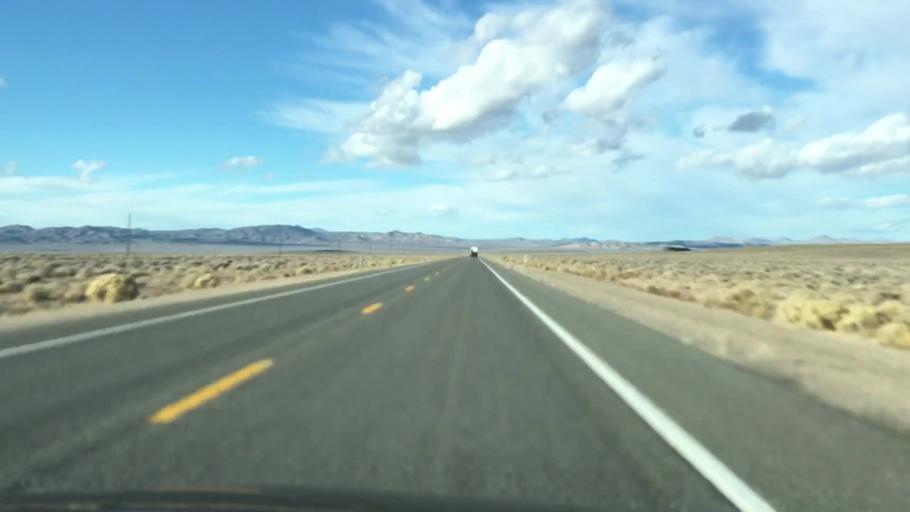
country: US
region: Nevada
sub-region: Esmeralda County
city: Goldfield
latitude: 37.4120
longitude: -117.1532
